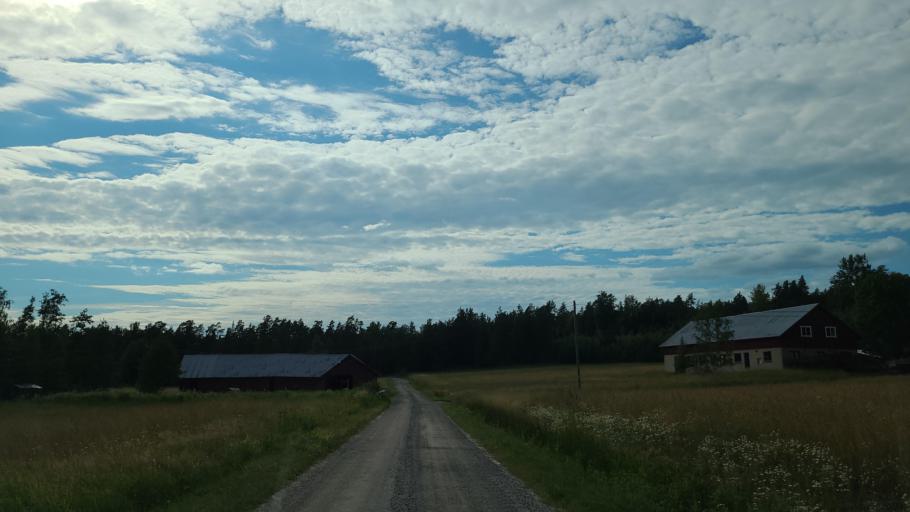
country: FI
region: Varsinais-Suomi
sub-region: Aboland-Turunmaa
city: Nagu
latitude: 60.2858
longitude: 21.9162
